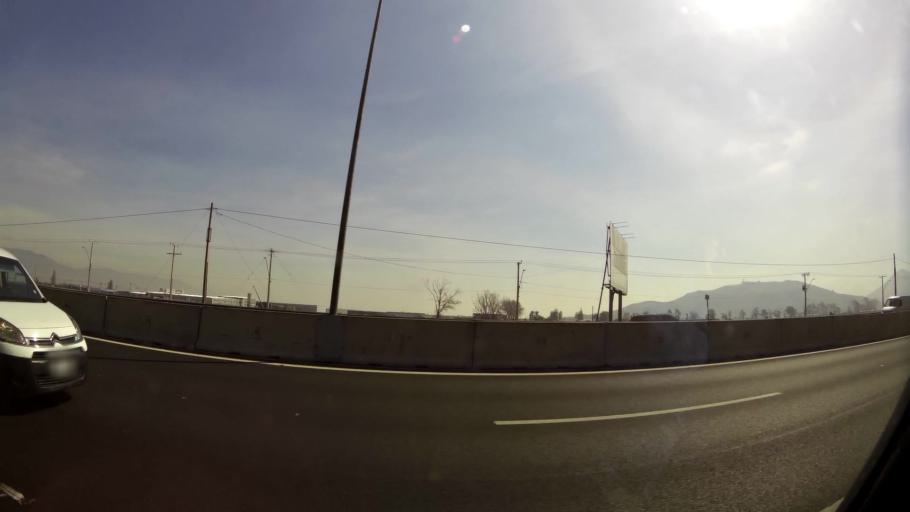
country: CL
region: Santiago Metropolitan
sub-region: Provincia de Santiago
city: Lo Prado
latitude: -33.4119
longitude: -70.7593
